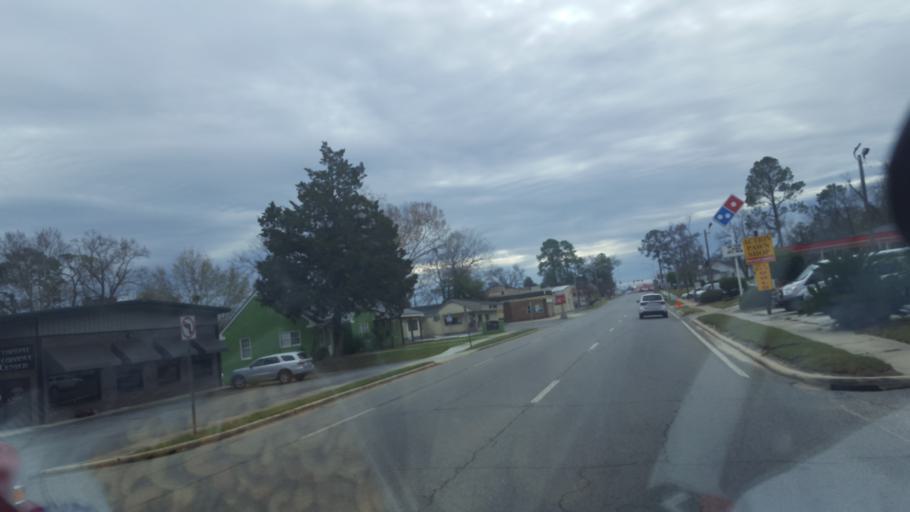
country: US
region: Georgia
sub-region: Ben Hill County
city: Fitzgerald
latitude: 31.7092
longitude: -83.2529
